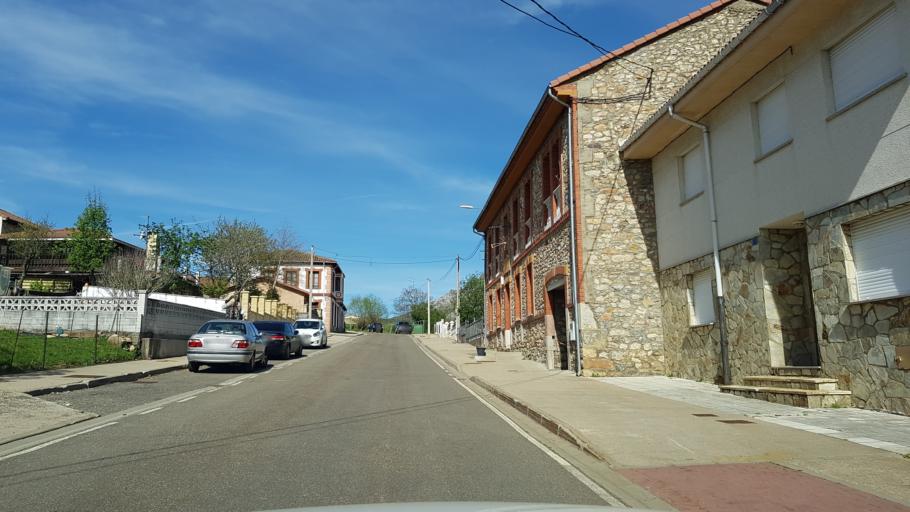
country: ES
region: Castille and Leon
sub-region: Provincia de Leon
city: Carmenes
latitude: 42.9589
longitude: -5.5753
